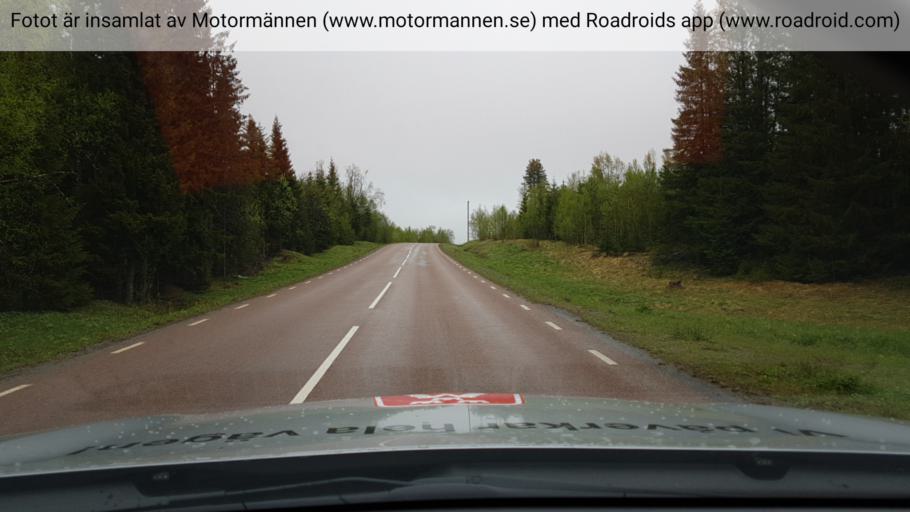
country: SE
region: Jaemtland
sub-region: Krokoms Kommun
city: Valla
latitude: 63.1656
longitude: 13.9931
